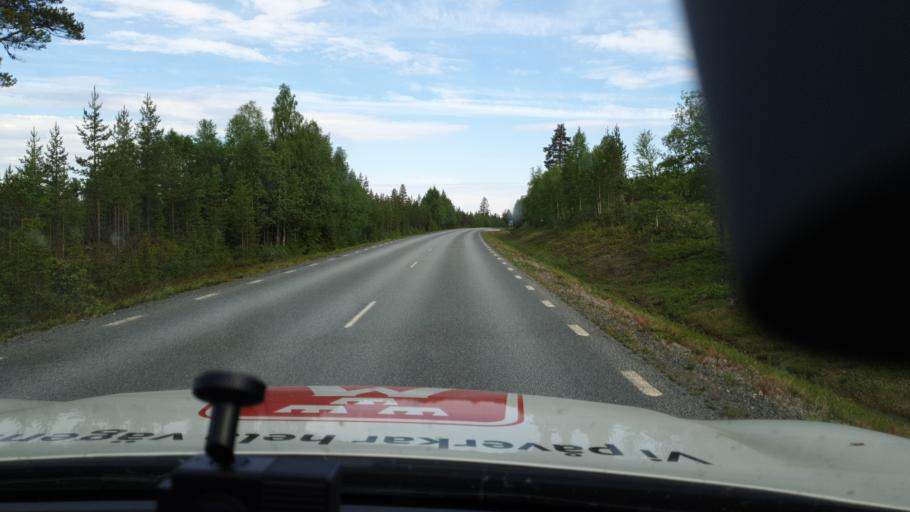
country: SE
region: Vaesterbotten
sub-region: Lycksele Kommun
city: Soderfors
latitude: 65.1383
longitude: 18.2679
